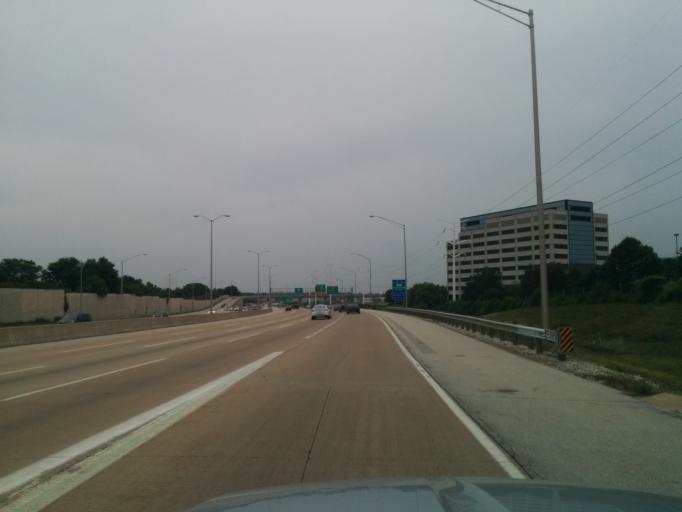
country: US
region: Illinois
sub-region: DuPage County
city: Downers Grove
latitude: 41.8287
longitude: -88.0210
